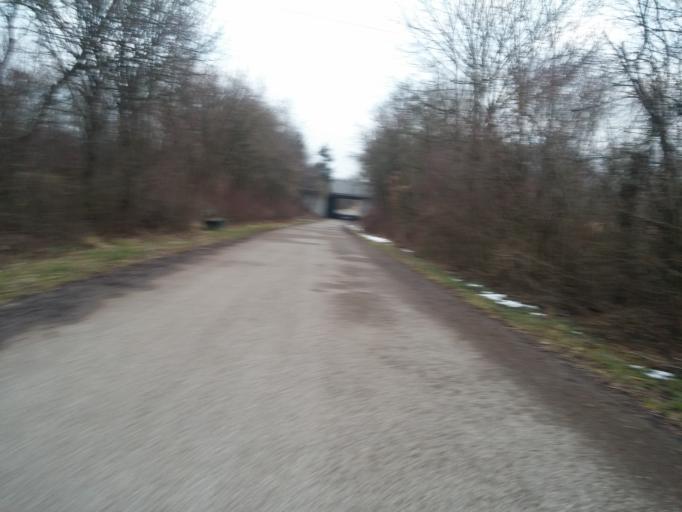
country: DE
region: Bavaria
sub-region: Upper Bavaria
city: Putzbrunn
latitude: 48.0696
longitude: 11.7187
